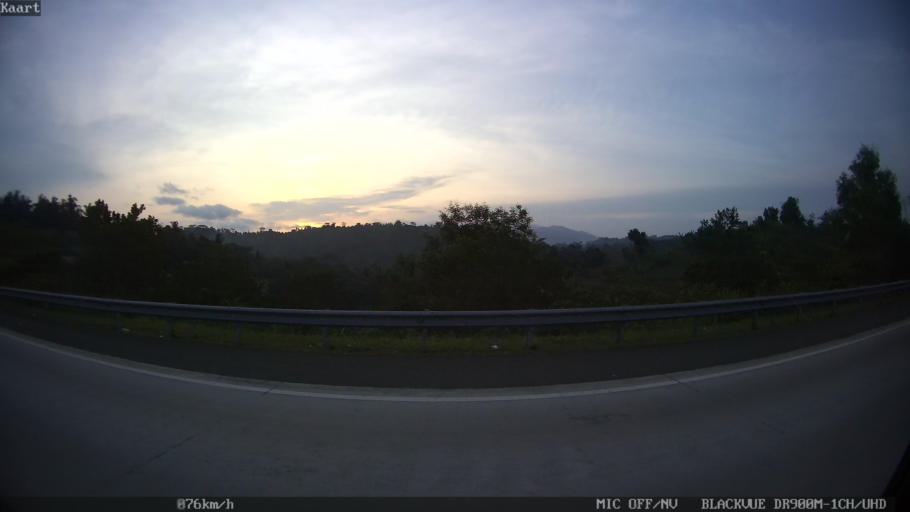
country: ID
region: Lampung
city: Penengahan
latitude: -5.8382
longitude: 105.7296
